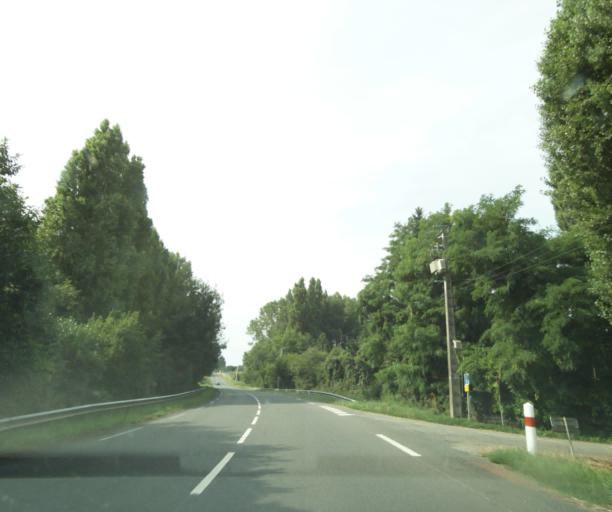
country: FR
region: Pays de la Loire
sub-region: Departement de la Sarthe
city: Marigne-Laille
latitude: 47.8079
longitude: 0.3138
